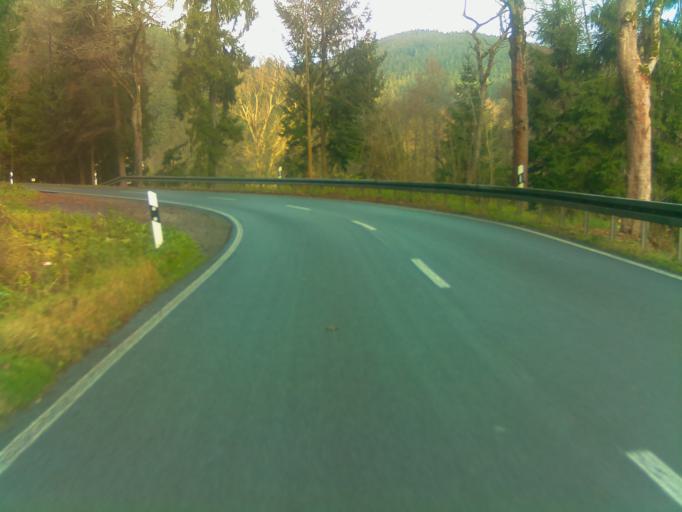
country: DE
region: Thuringia
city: Wildenspring
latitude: 50.5954
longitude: 11.0820
